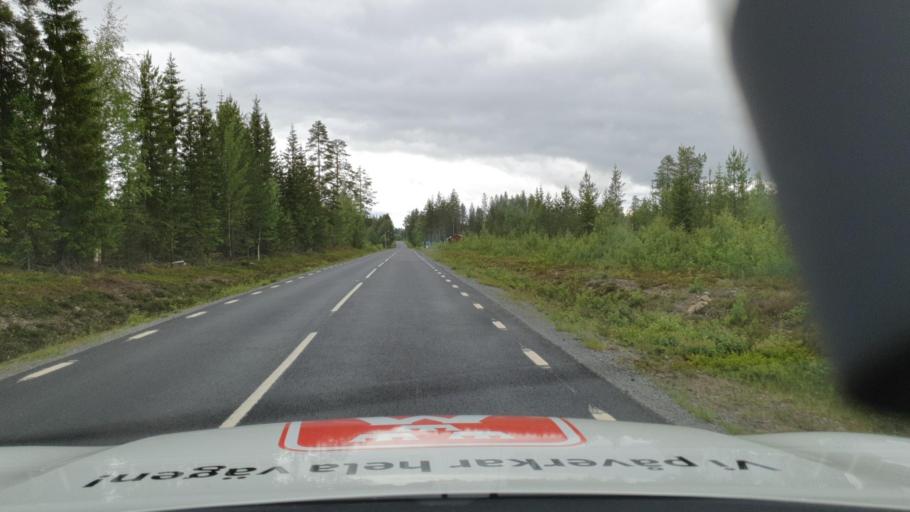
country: SE
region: Vaesterbotten
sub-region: Dorotea Kommun
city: Dorotea
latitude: 64.2109
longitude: 16.5554
